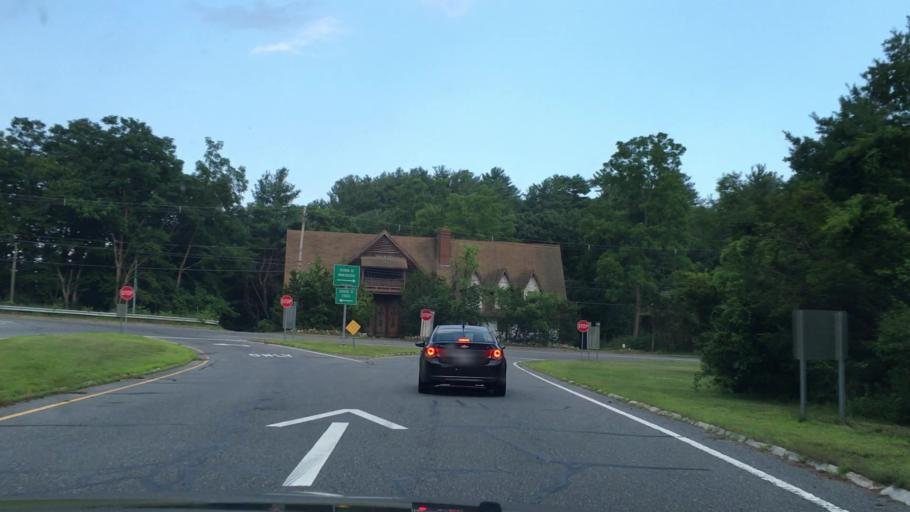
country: US
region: Massachusetts
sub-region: Essex County
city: Essex
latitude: 42.5890
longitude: -70.7666
